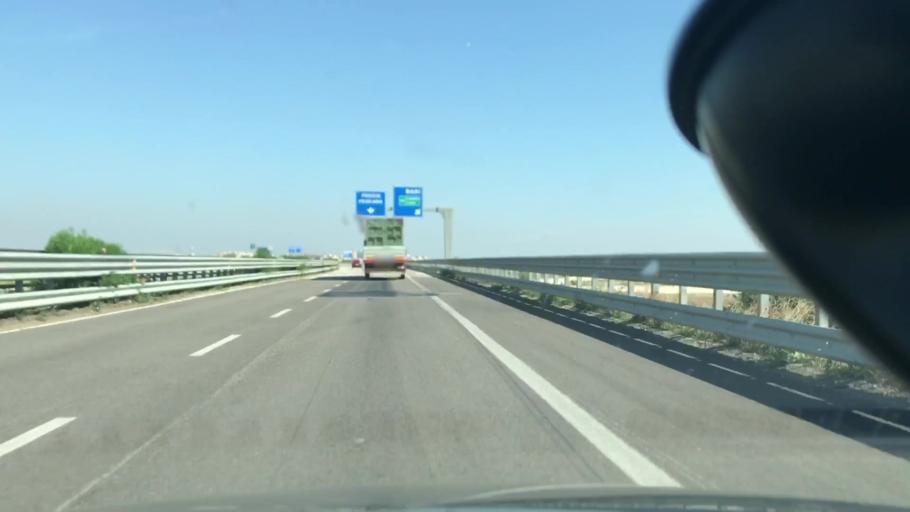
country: IT
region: Apulia
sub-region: Provincia di Foggia
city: Foggia
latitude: 41.4216
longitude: 15.5590
